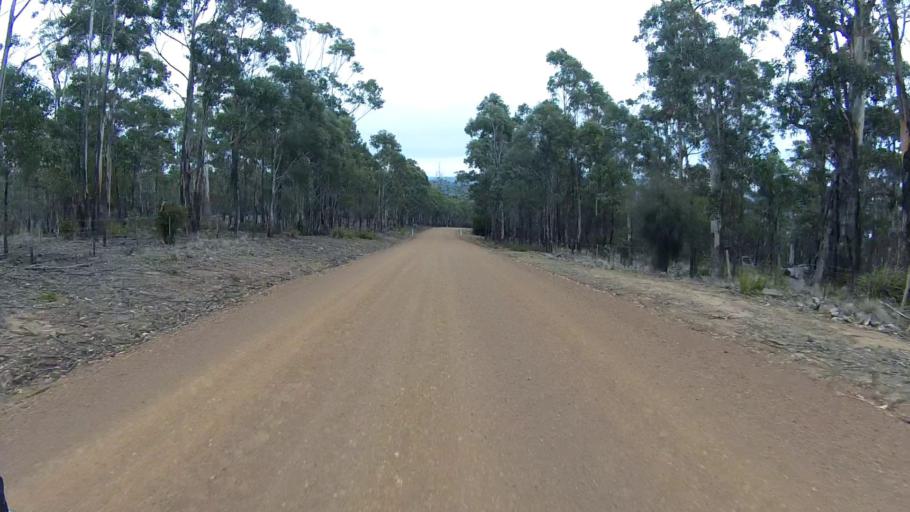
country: AU
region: Tasmania
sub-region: Sorell
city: Sorell
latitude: -42.5845
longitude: 147.8827
